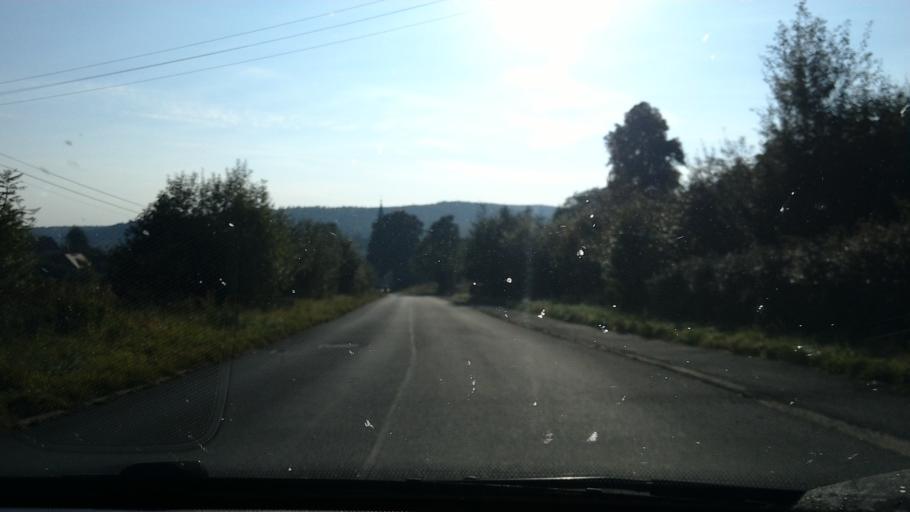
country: PL
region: Lower Silesian Voivodeship
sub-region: Powiat jeleniogorski
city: Szklarska Poreba
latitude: 50.8423
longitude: 15.5491
